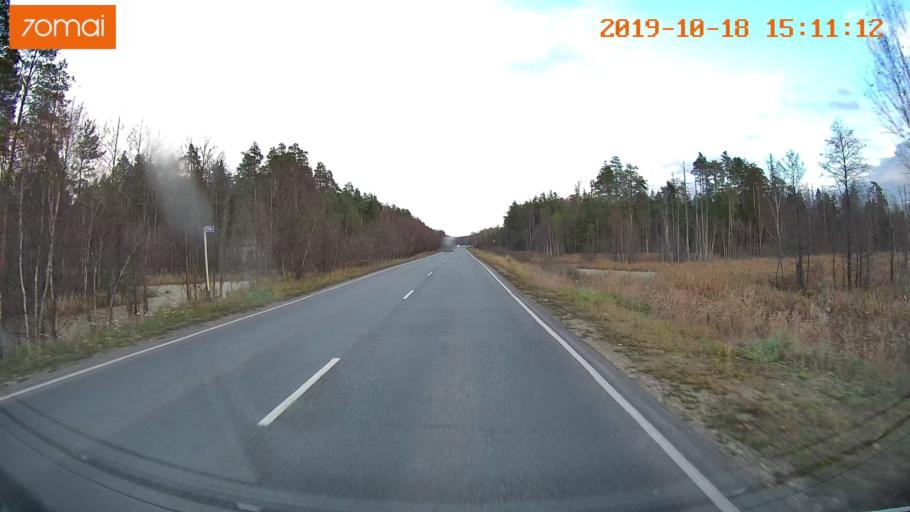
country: RU
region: Vladimir
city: Gus'-Khrustal'nyy
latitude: 55.5707
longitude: 40.6648
